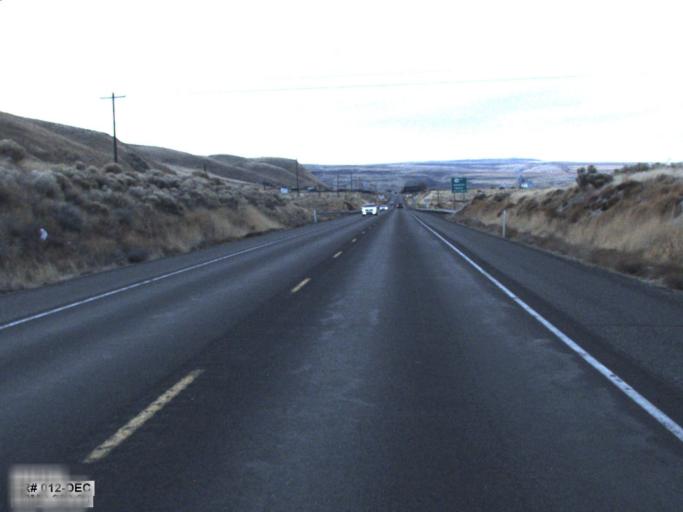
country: US
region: Washington
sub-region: Benton County
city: Finley
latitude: 46.0539
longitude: -118.8876
